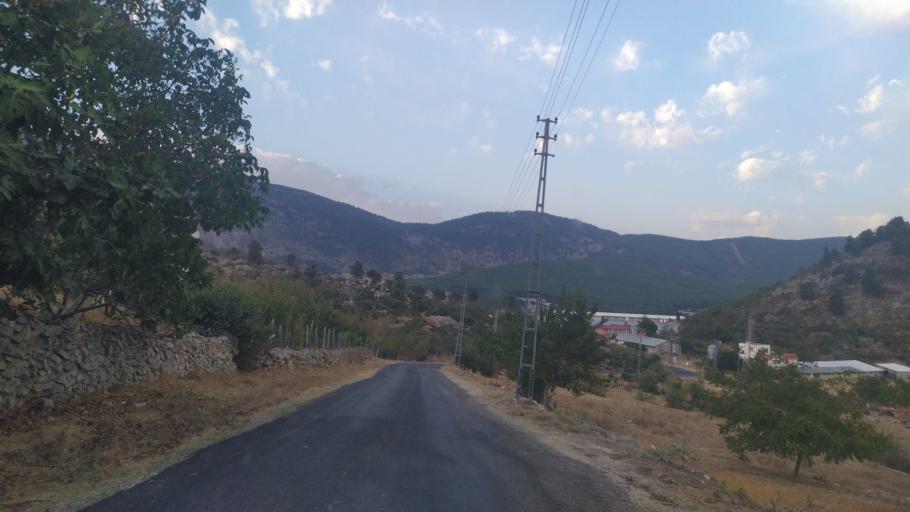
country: TR
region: Mersin
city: Camliyayla
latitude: 37.2315
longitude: 34.7153
